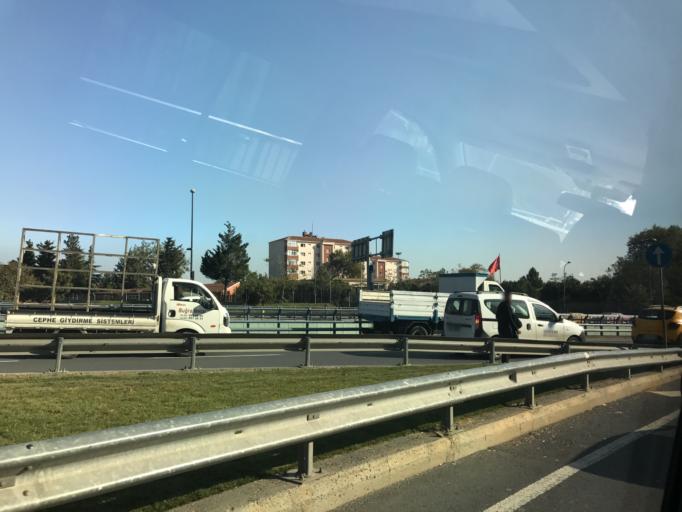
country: TR
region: Istanbul
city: Sisli
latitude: 41.0650
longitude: 29.0120
